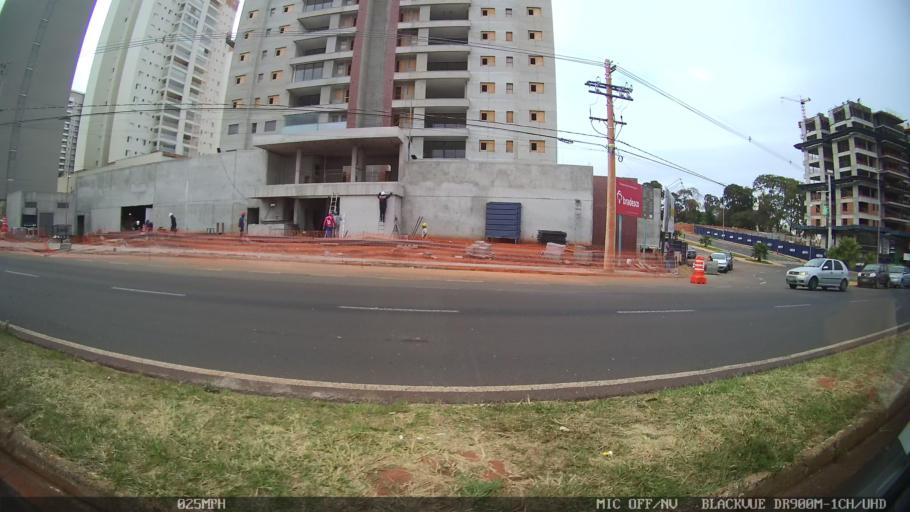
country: BR
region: Sao Paulo
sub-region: Sao Jose Do Rio Preto
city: Sao Jose do Rio Preto
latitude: -20.8282
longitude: -49.3848
